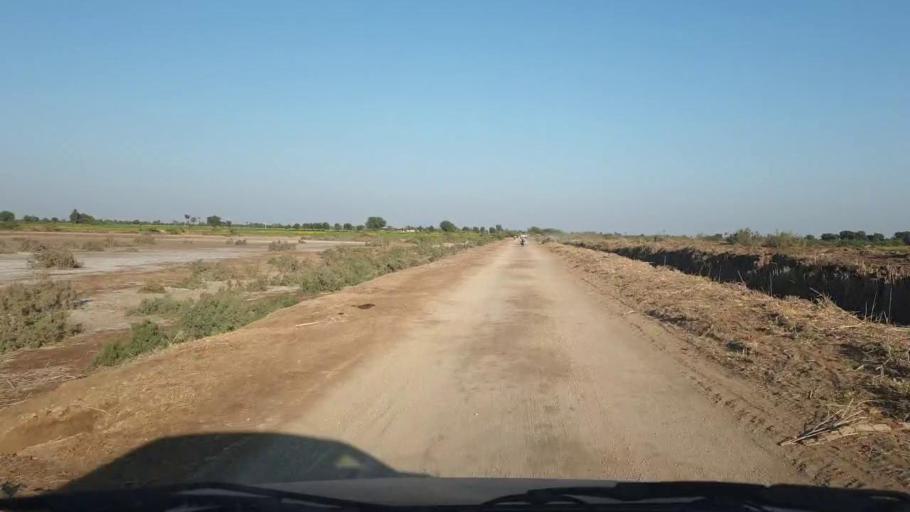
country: PK
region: Sindh
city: Samaro
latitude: 25.3261
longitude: 69.3059
